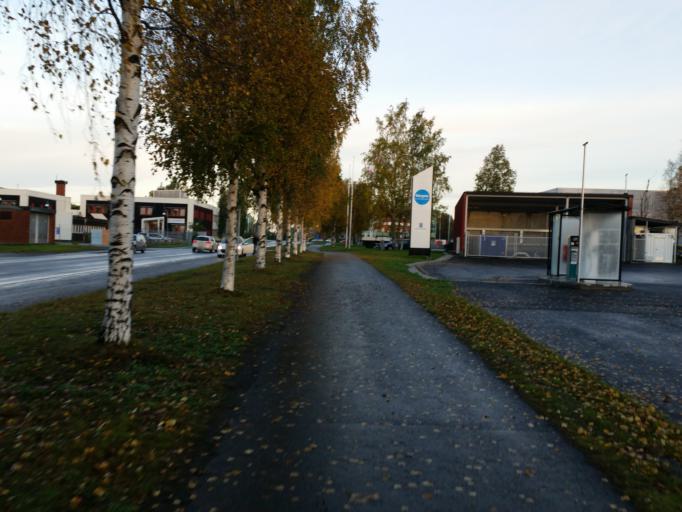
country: SE
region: Norrbotten
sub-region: Lulea Kommun
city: Lulea
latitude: 65.6013
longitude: 22.1401
